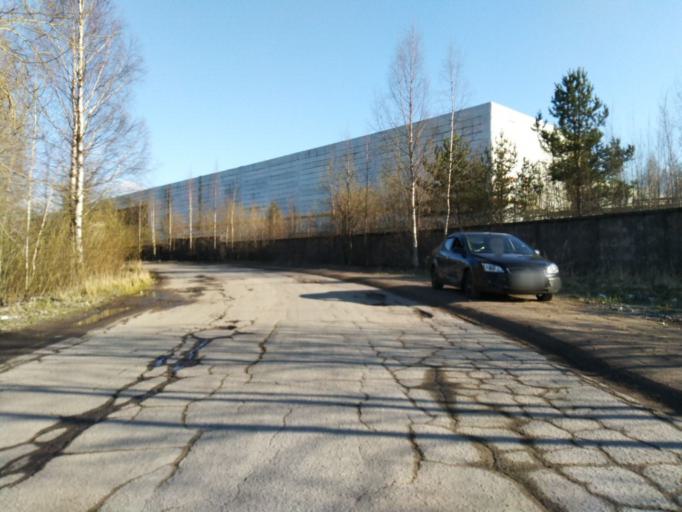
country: RU
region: Leningrad
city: Novoye Devyatkino
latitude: 60.0681
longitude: 30.4800
